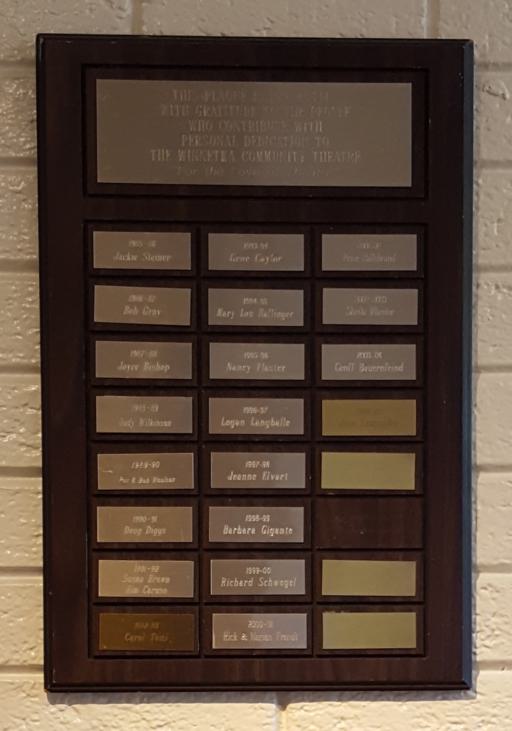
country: US
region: Illinois
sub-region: Cook County
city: Winnetka
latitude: 42.1083
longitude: -87.7335
